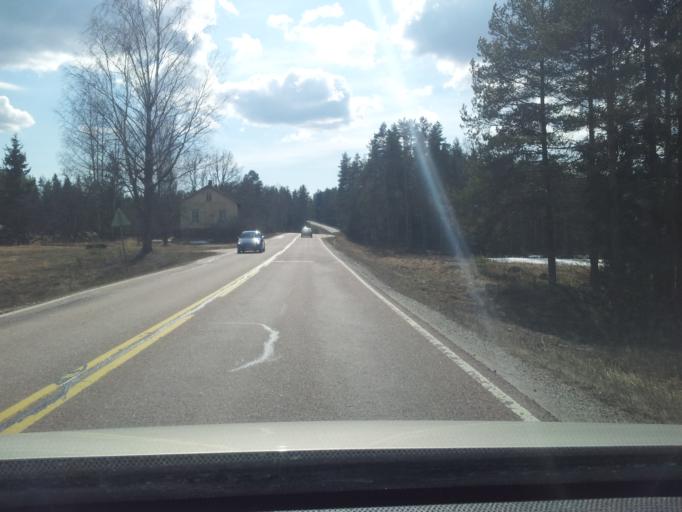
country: FI
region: South Karelia
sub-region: Lappeenranta
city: Taavetti
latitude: 60.8682
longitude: 27.4264
